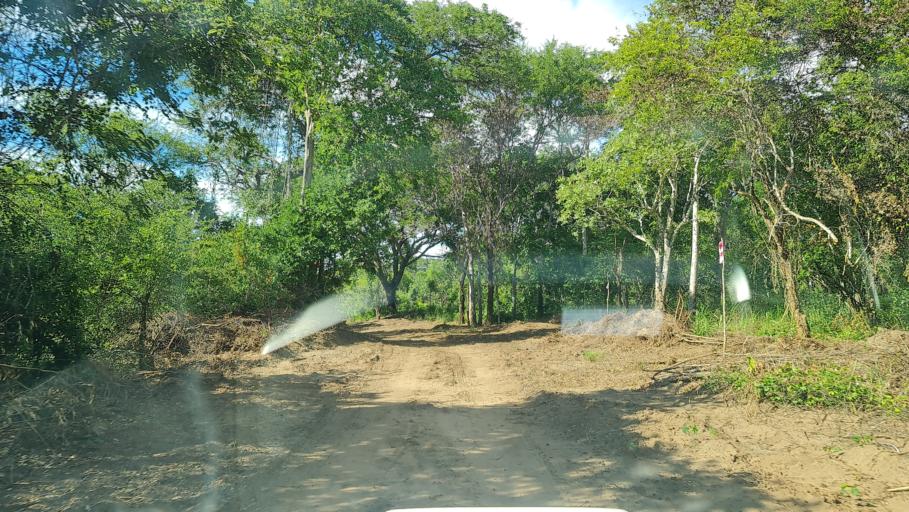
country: MZ
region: Nampula
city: Antonio Enes
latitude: -15.5276
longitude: 40.1268
